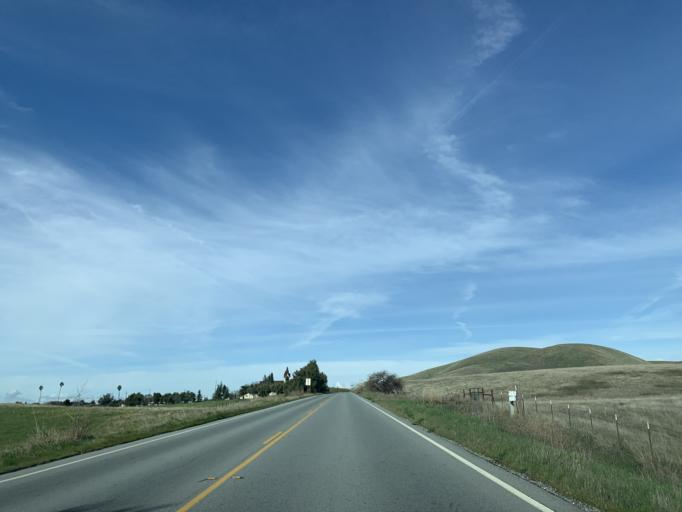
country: US
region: California
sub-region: San Benito County
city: Ridgemark
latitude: 36.7838
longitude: -121.3143
